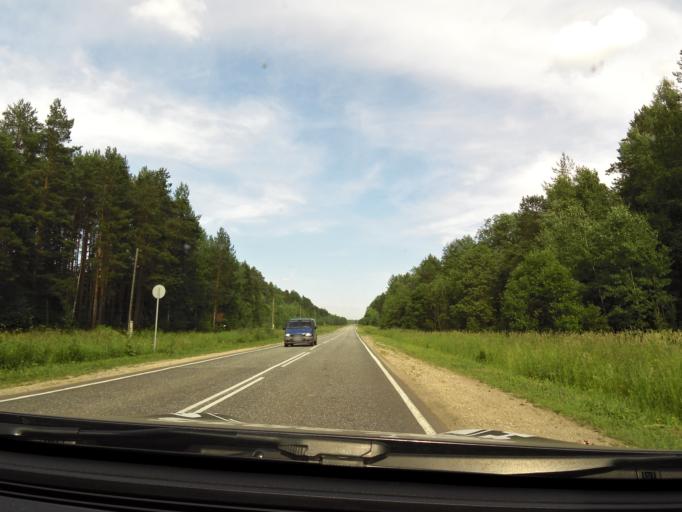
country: RU
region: Kirov
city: Slobodskoy
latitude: 58.7753
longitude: 50.3848
